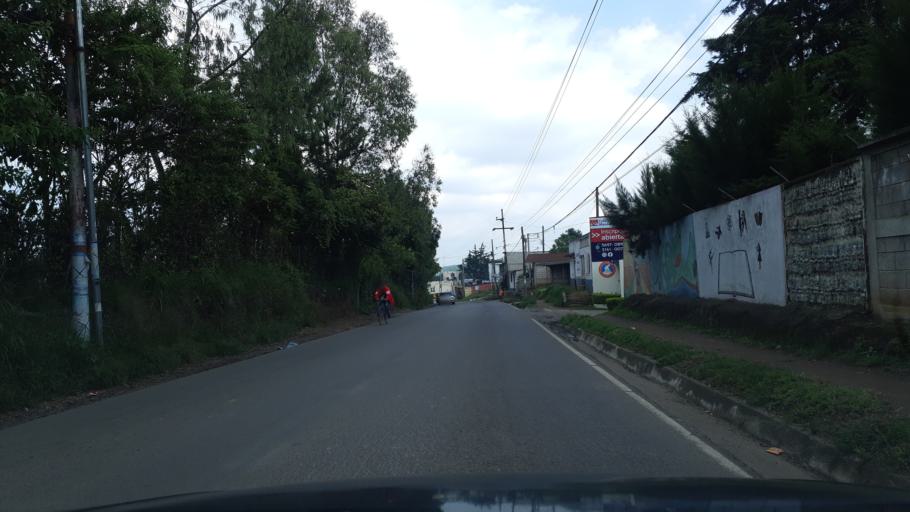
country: GT
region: Chimaltenango
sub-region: Municipio de Chimaltenango
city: Chimaltenango
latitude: 14.6736
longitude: -90.8044
